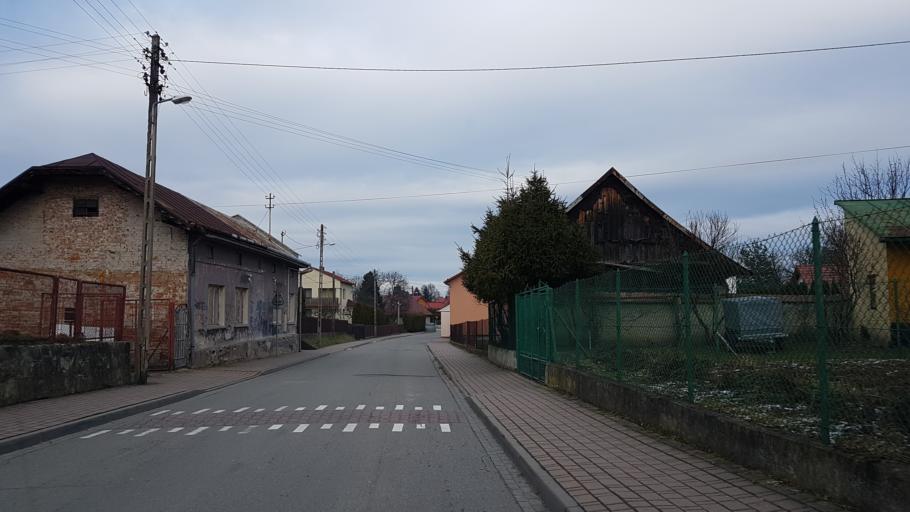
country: PL
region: Lesser Poland Voivodeship
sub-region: Powiat nowosadecki
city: Stary Sacz
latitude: 49.5582
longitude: 20.6337
